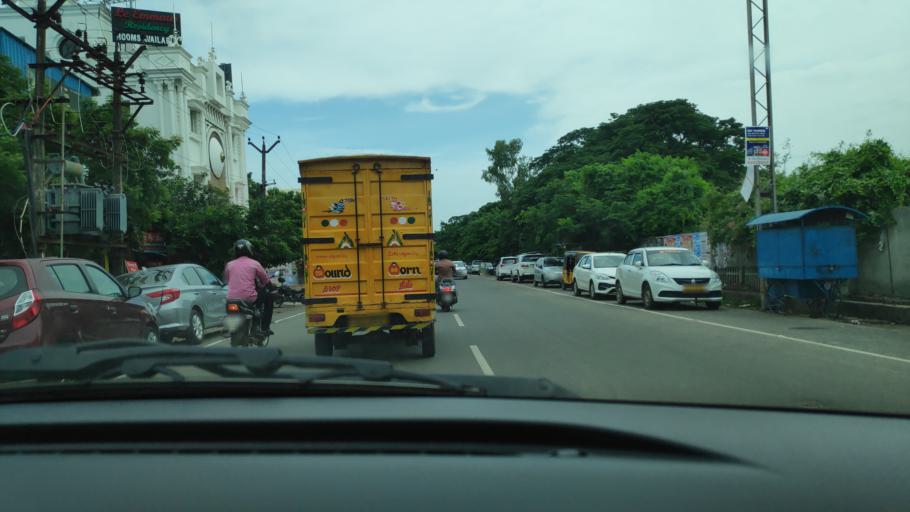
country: IN
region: Tamil Nadu
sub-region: Kancheepuram
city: Pallavaram
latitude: 12.9263
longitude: 80.1265
